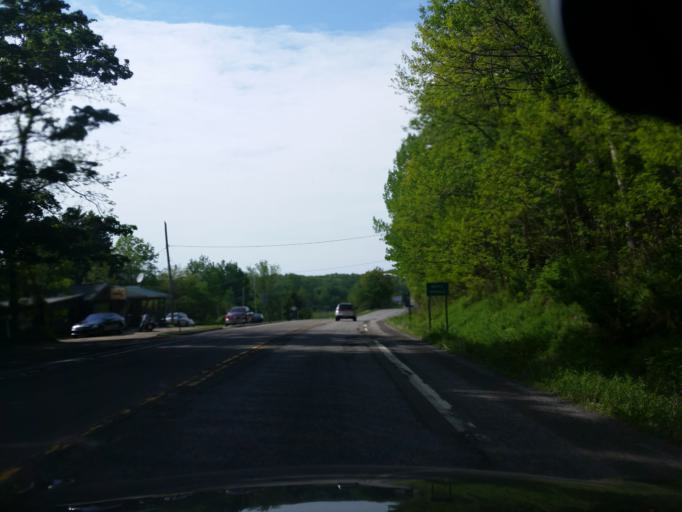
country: US
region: New York
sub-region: Chautauqua County
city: Mayville
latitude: 42.1945
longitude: -79.4151
